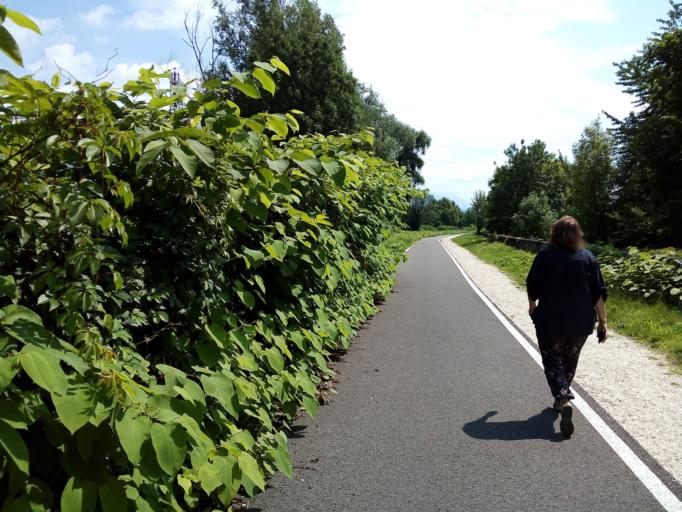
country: FR
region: Rhone-Alpes
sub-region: Departement de l'Isere
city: La Tronche
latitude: 45.1969
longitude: 5.7438
